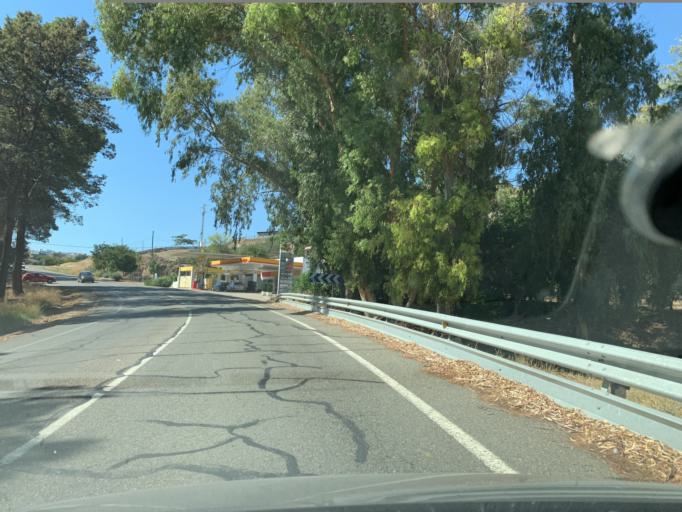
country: ES
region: Andalusia
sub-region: Provincia de Sevilla
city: Carmona
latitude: 37.4688
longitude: -5.6324
